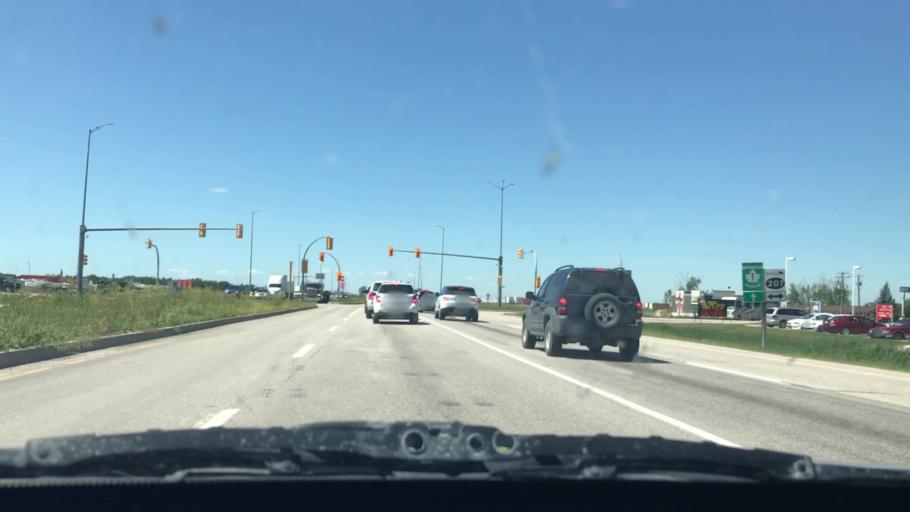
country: CA
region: Manitoba
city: Winnipeg
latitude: 49.8196
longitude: -96.9346
